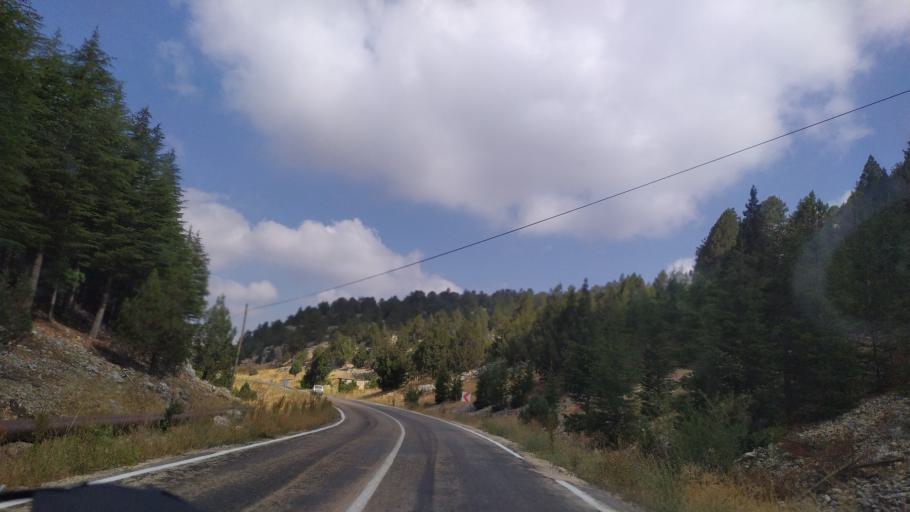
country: TR
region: Mersin
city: Kirobasi
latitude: 36.6136
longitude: 33.8790
